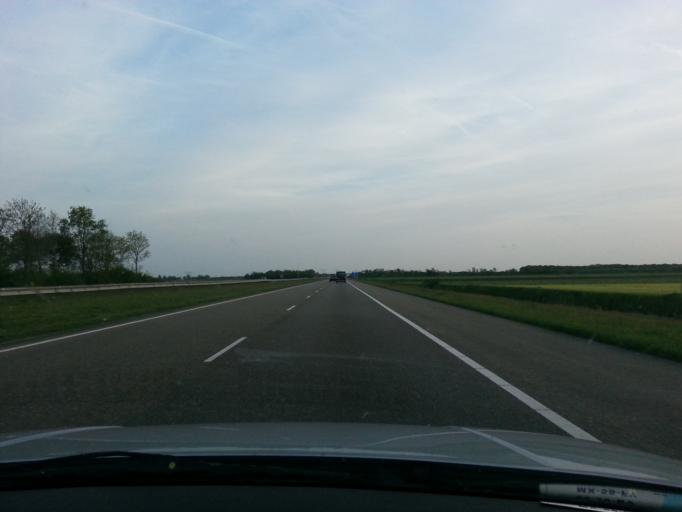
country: NL
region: Friesland
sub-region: Gemeente Skarsterlan
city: Joure
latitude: 52.9317
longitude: 5.7829
